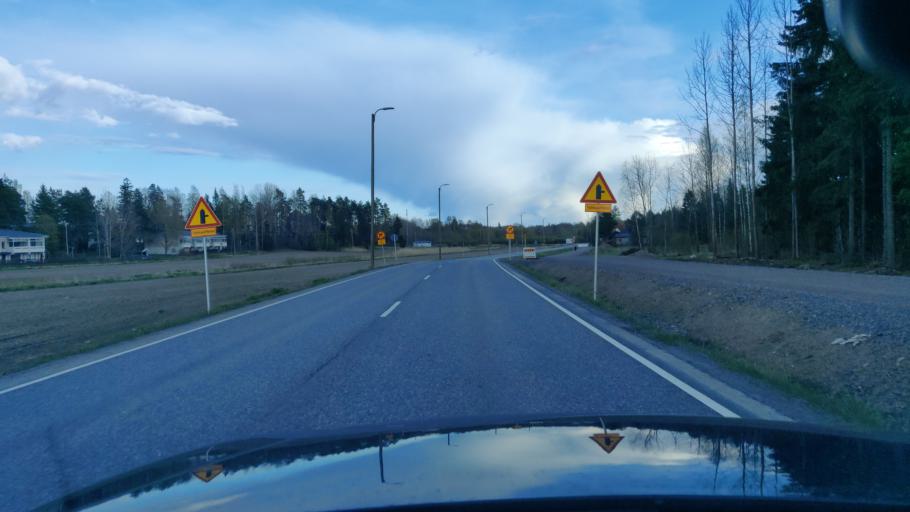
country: FI
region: Uusimaa
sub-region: Helsinki
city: Jaervenpaeae
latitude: 60.4727
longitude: 25.0684
